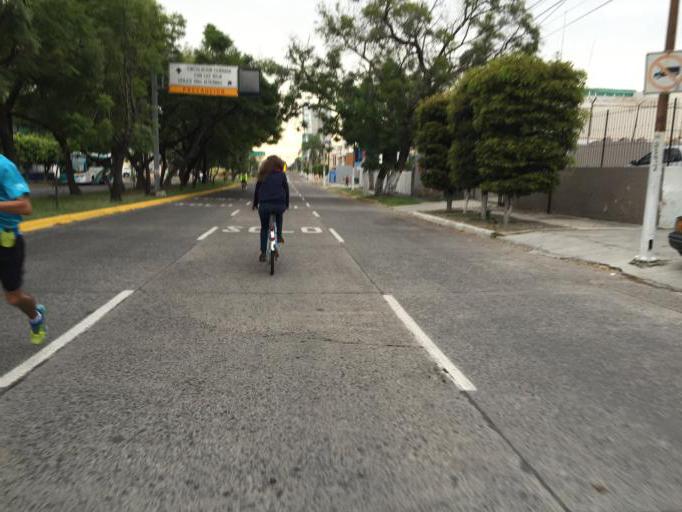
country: MX
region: Jalisco
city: Guadalajara
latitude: 20.6666
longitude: -103.3825
